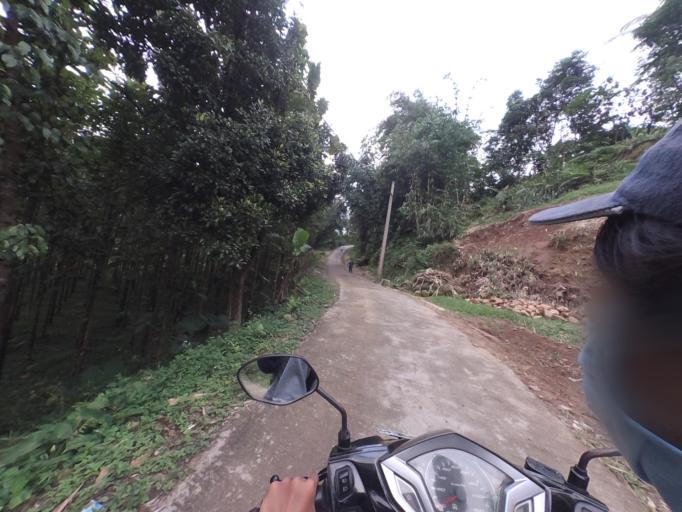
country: ID
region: West Java
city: Ciampea
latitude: -6.6834
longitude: 106.6606
